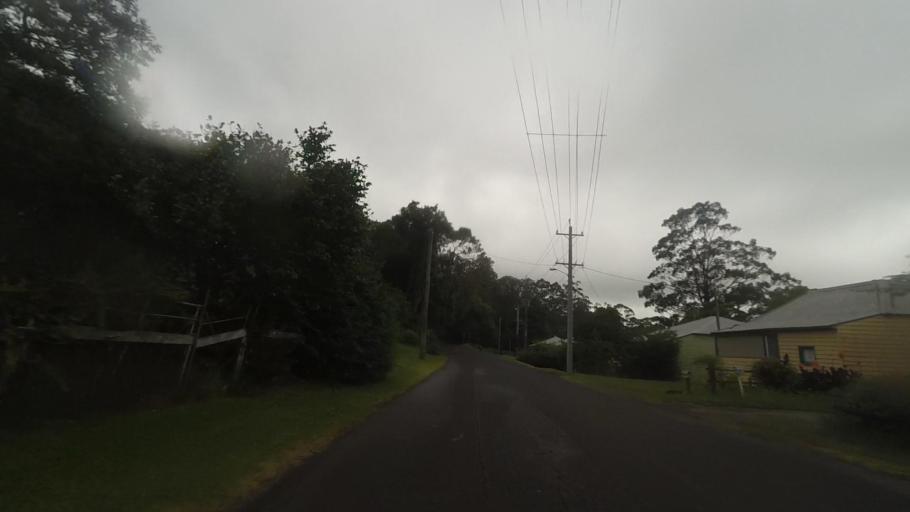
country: AU
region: New South Wales
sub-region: Wollongong
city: Cordeaux Heights
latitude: -34.4283
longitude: 150.8090
